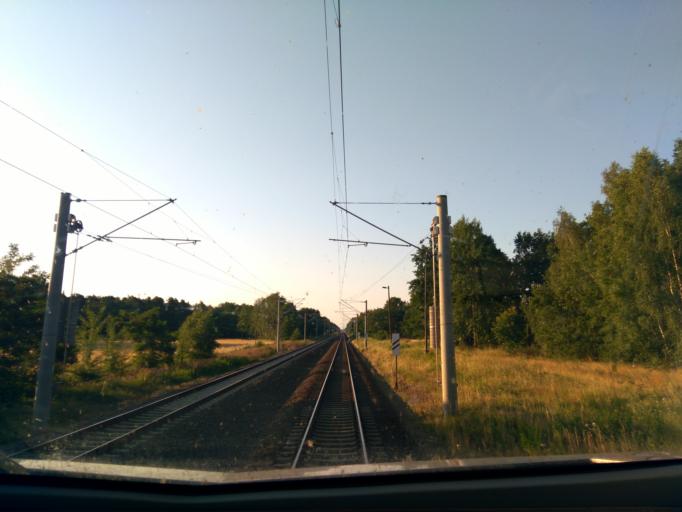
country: DE
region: Brandenburg
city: Kasel-Golzig
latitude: 51.9901
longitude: 13.7789
